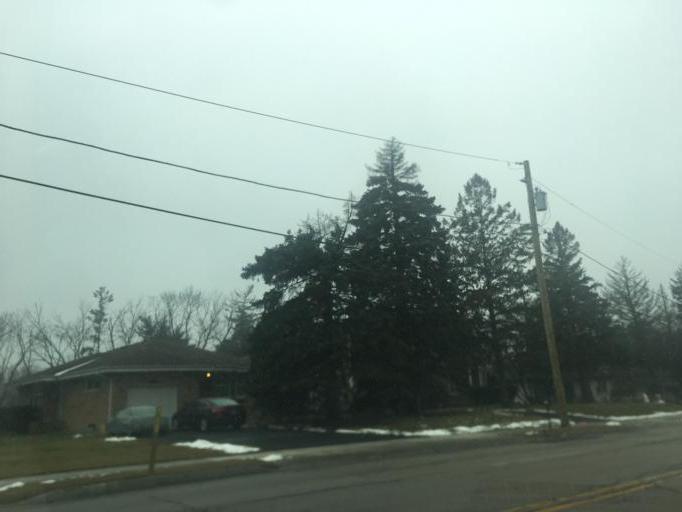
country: US
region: Illinois
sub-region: DuPage County
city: Westmont
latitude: 41.7882
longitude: -87.9850
